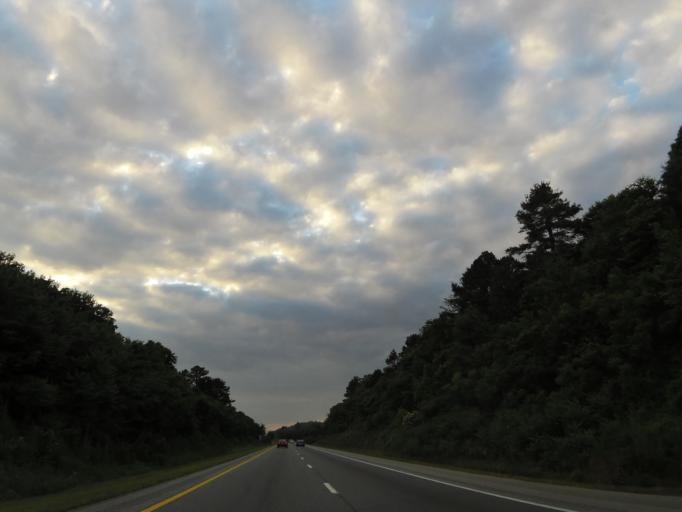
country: US
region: Tennessee
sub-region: Smith County
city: Gordonsville
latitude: 36.1575
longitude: -85.8797
